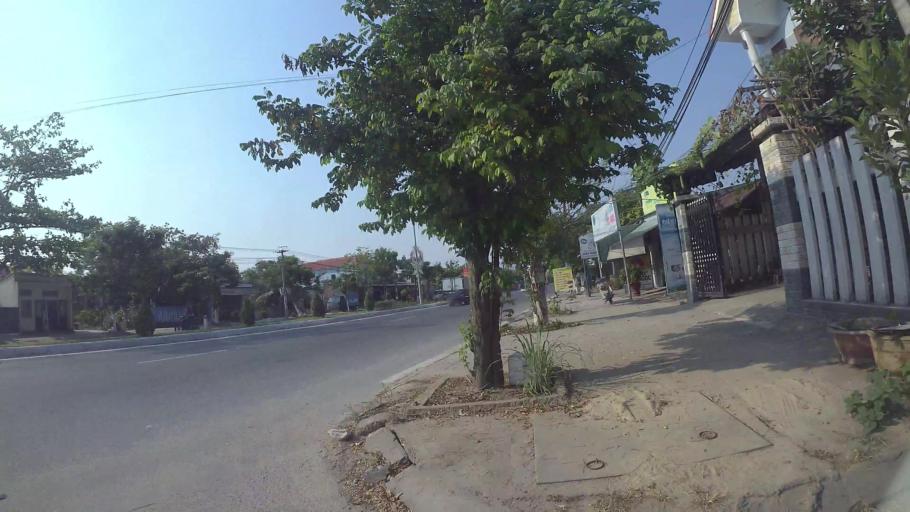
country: VN
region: Quang Nam
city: Quang Nam
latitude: 15.9512
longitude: 108.2548
